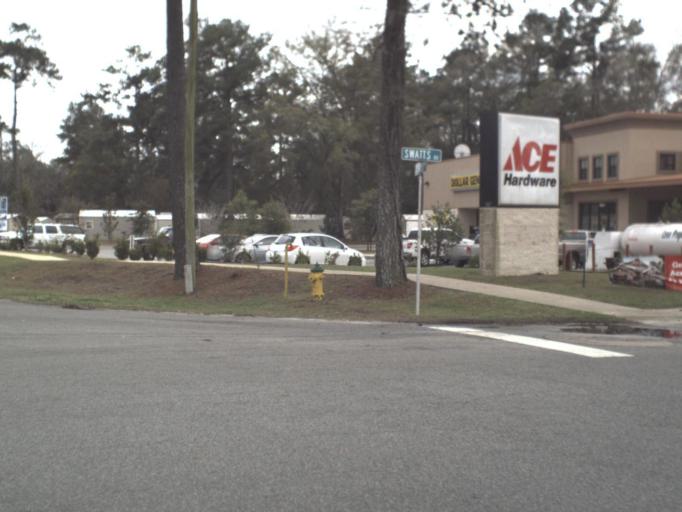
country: US
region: Florida
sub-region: Leon County
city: Tallahassee
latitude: 30.5007
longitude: -84.3285
